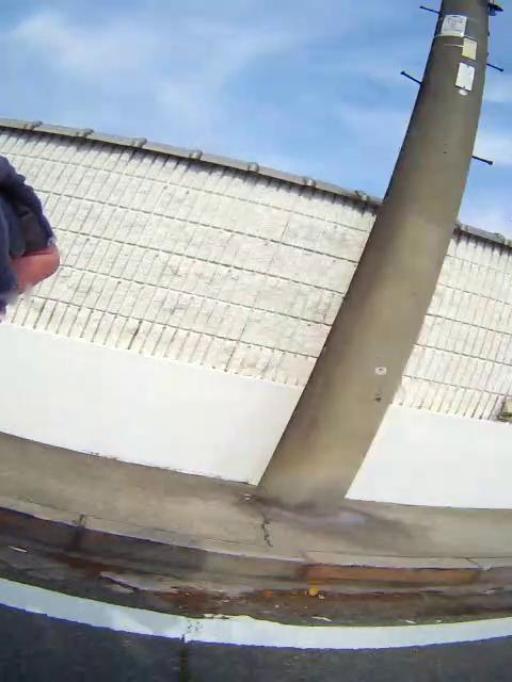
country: JP
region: Osaka
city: Toyonaka
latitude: 34.7822
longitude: 135.4862
